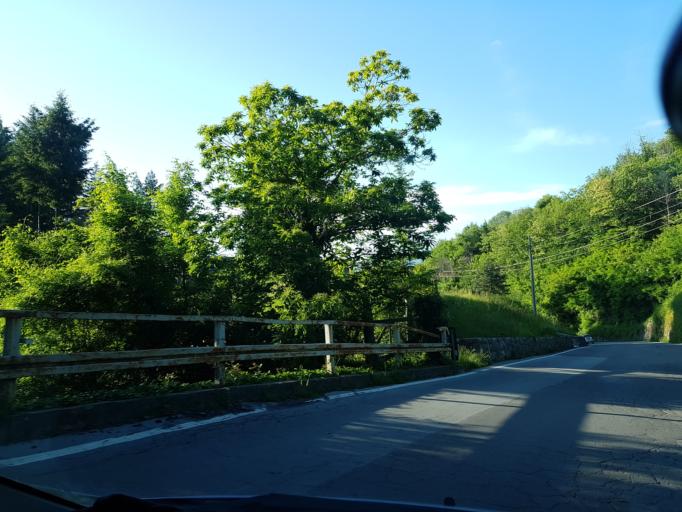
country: IT
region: Tuscany
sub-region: Provincia di Lucca
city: Minucciano
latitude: 44.1665
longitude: 10.2094
